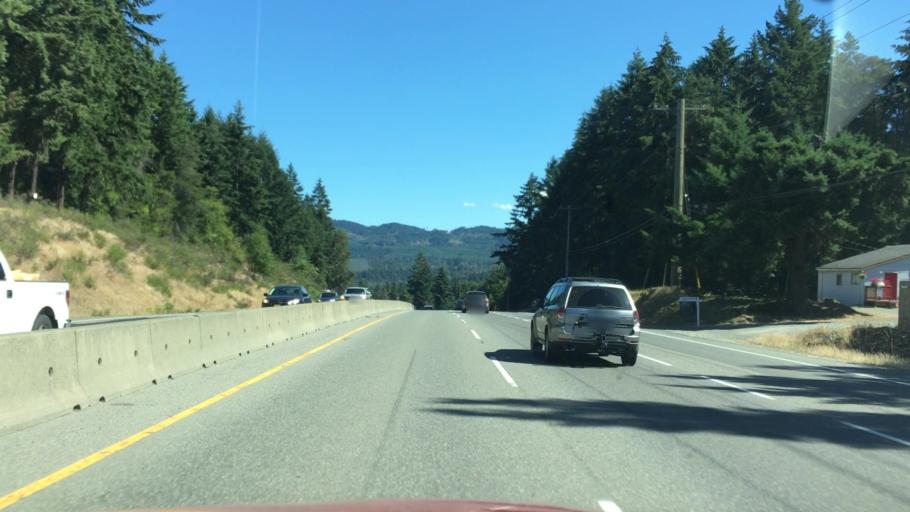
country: CA
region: British Columbia
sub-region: Regional District of Nanaimo
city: Parksville
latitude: 49.2732
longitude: -124.2363
